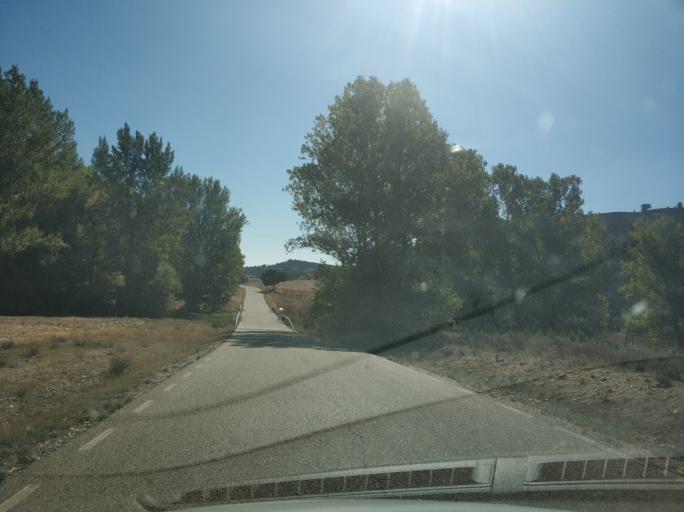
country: ES
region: Castille and Leon
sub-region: Provincia de Soria
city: Espeja de San Marcelino
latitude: 41.7871
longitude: -3.1998
